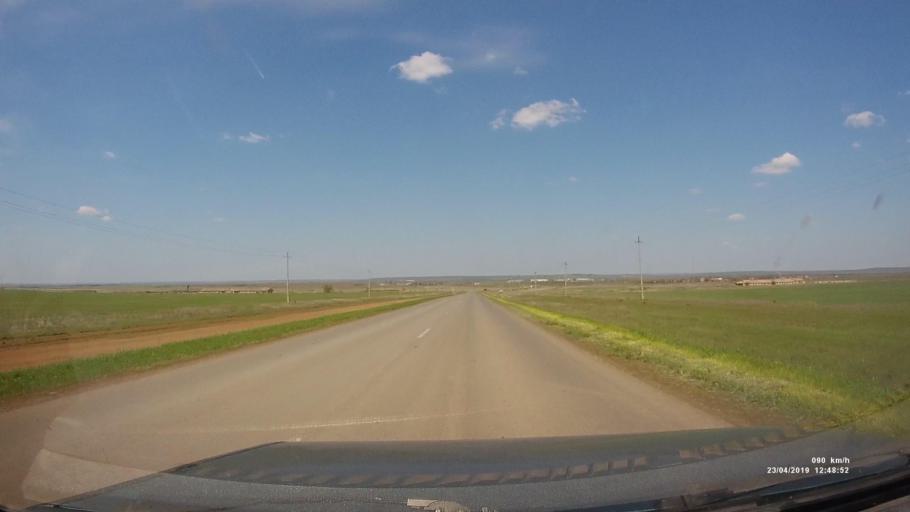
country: RU
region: Kalmykiya
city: Yashalta
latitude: 46.5300
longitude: 42.6389
